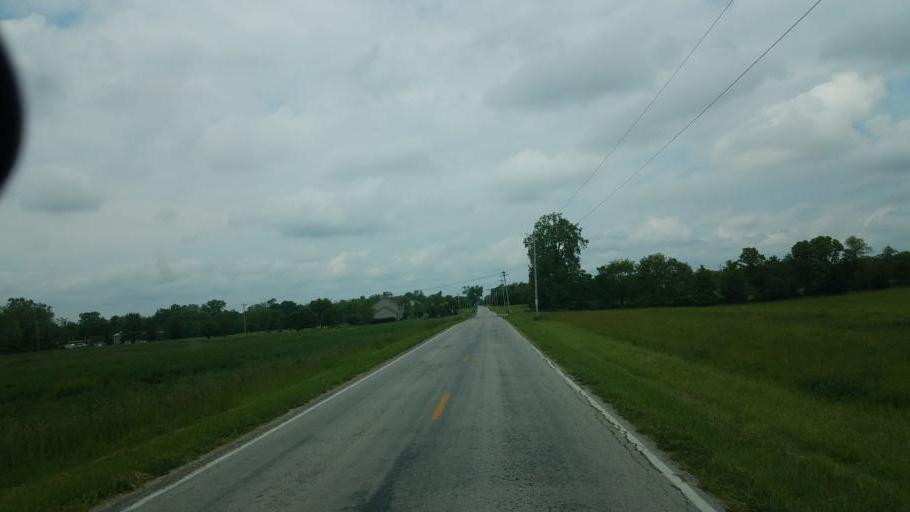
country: US
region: Ohio
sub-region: Marion County
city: Prospect
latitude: 40.3482
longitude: -83.1773
